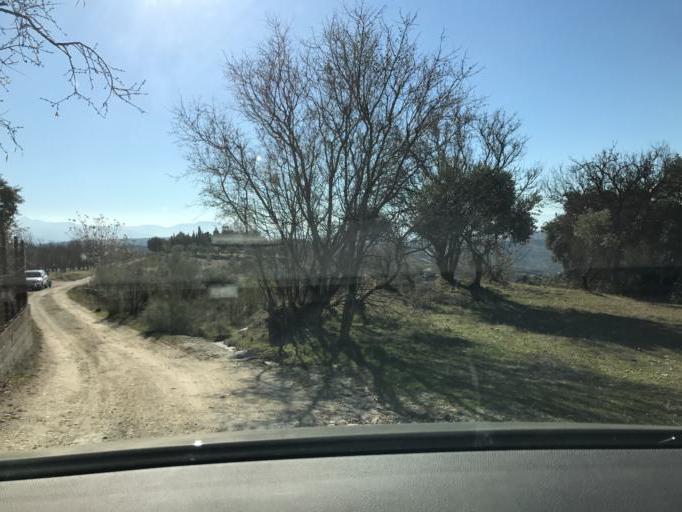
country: ES
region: Andalusia
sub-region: Provincia de Granada
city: Viznar
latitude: 37.2166
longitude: -3.5550
